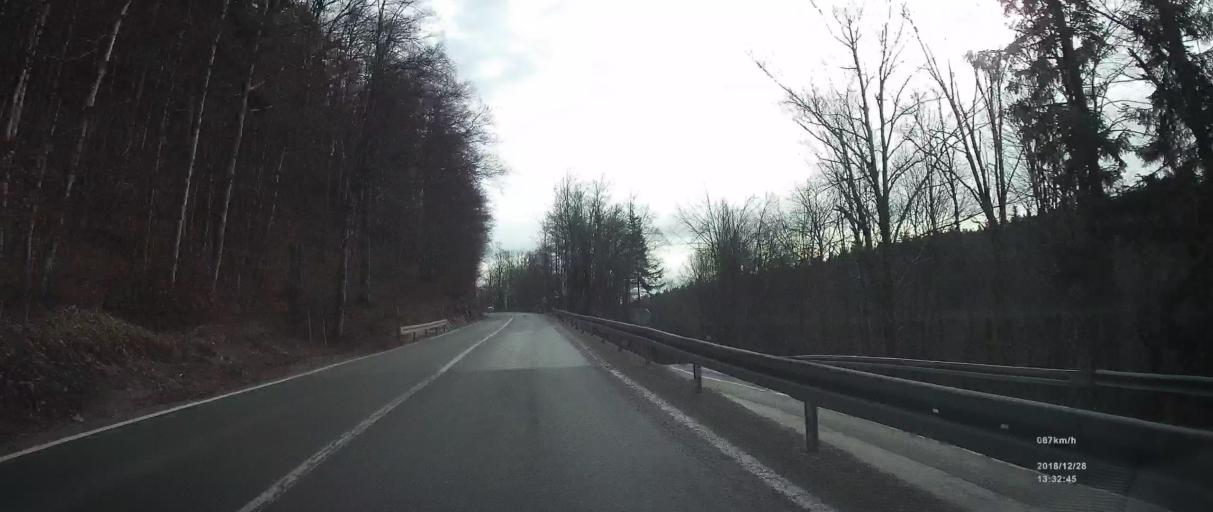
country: HR
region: Primorsko-Goranska
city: Hreljin
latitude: 45.3444
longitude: 14.6690
